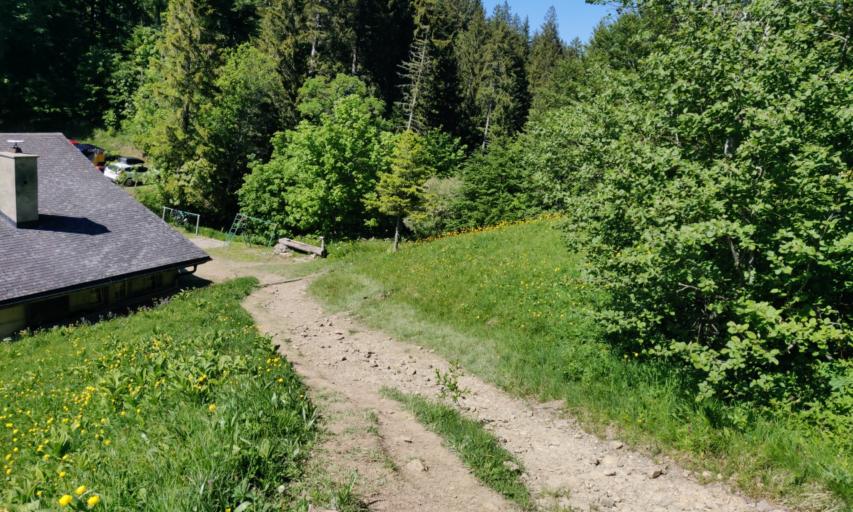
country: CH
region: Schwyz
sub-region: Bezirk Schwyz
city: Goldau
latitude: 47.0181
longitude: 8.5514
